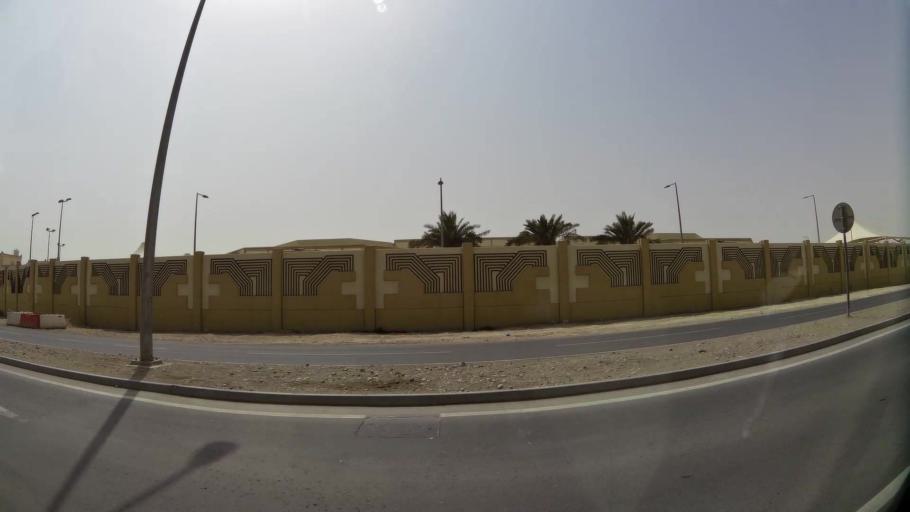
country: QA
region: Baladiyat ar Rayyan
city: Ar Rayyan
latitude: 25.2342
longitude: 51.3834
